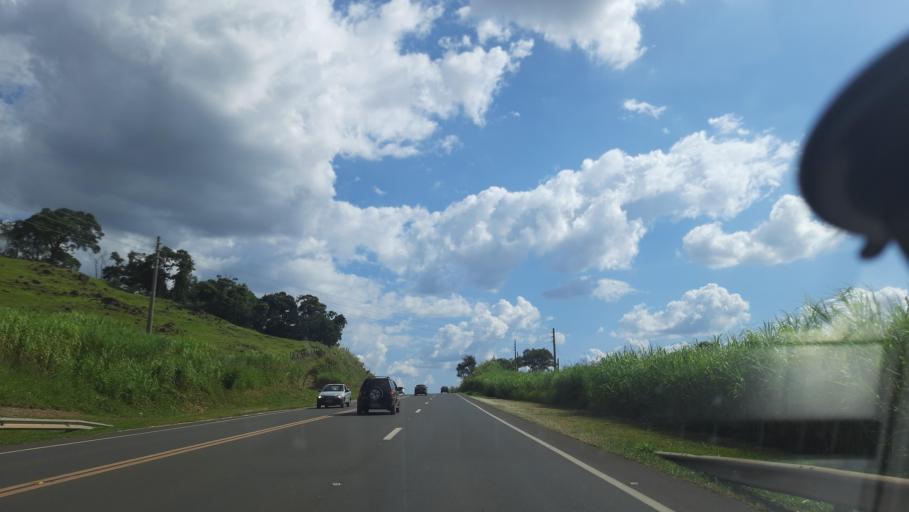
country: BR
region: Sao Paulo
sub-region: Sao Jose Do Rio Pardo
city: Sao Jose do Rio Pardo
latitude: -21.6561
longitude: -46.9146
